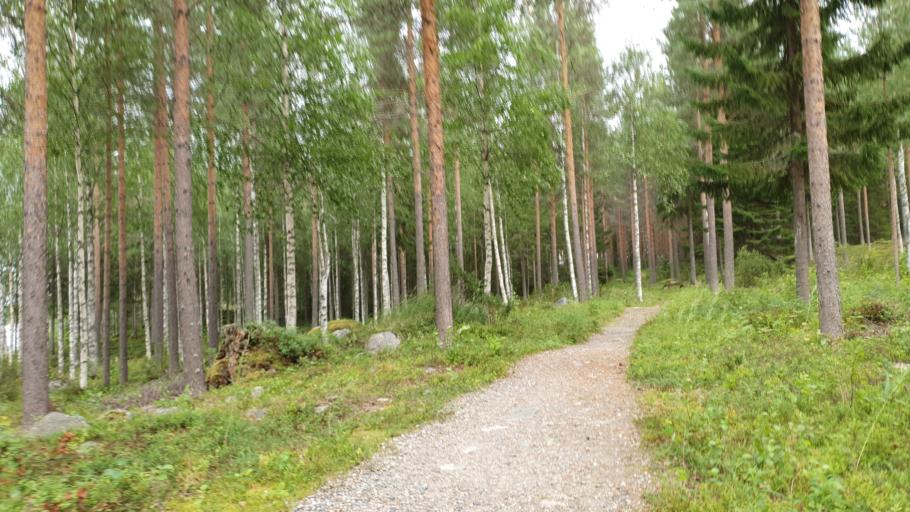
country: FI
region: Kainuu
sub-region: Kehys-Kainuu
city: Kuhmo
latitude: 64.1377
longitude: 29.4631
